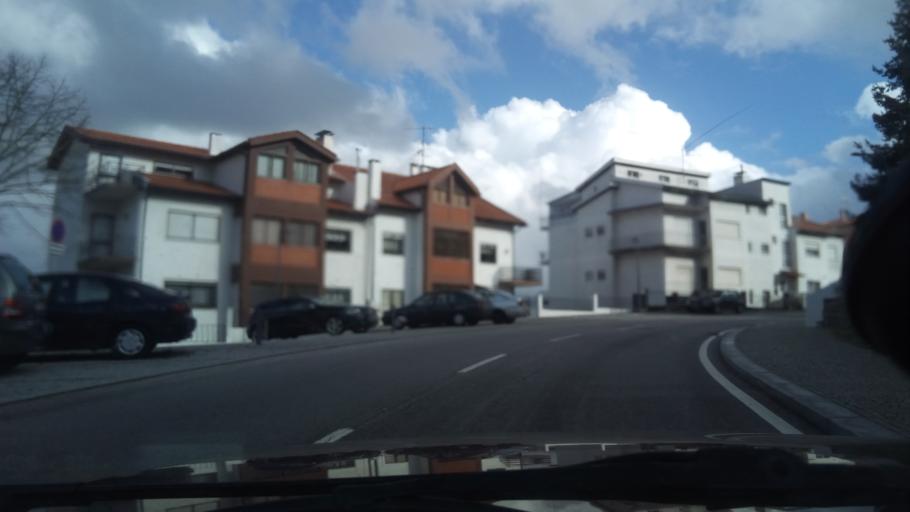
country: PT
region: Guarda
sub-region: Guarda
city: Guarda
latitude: 40.5378
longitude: -7.2620
